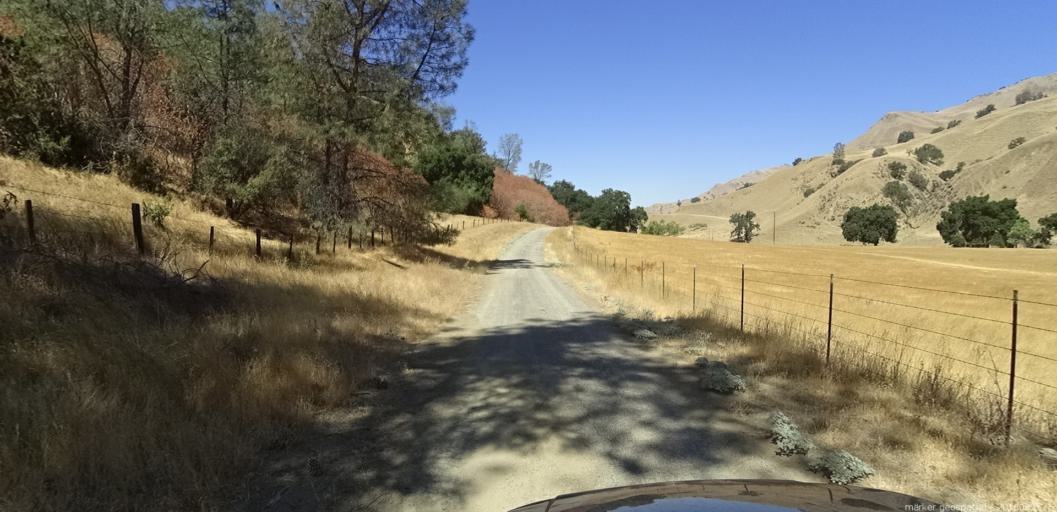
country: US
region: California
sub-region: Monterey County
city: King City
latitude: 36.2795
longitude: -120.8458
